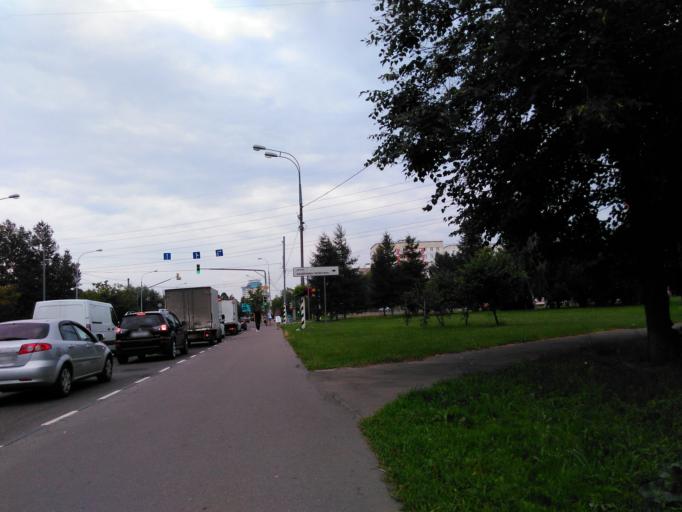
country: RU
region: Moskovskaya
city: Semenovskoye
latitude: 55.6740
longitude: 37.5432
